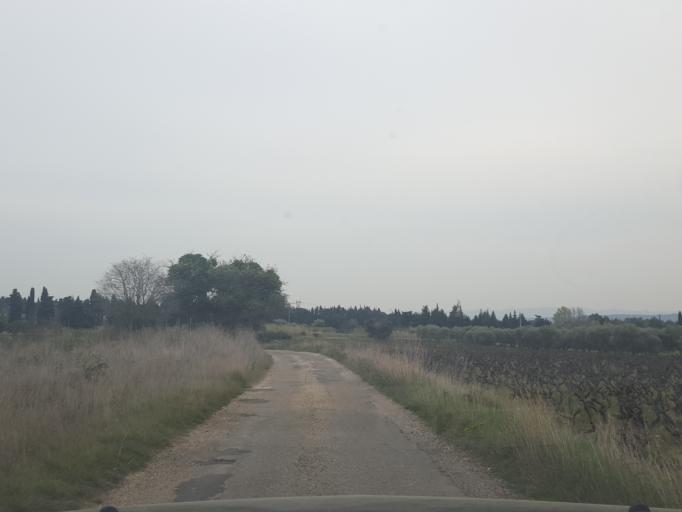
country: FR
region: Provence-Alpes-Cote d'Azur
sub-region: Departement du Vaucluse
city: Saint-Saturnin-les-Avignon
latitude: 43.9533
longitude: 4.9132
